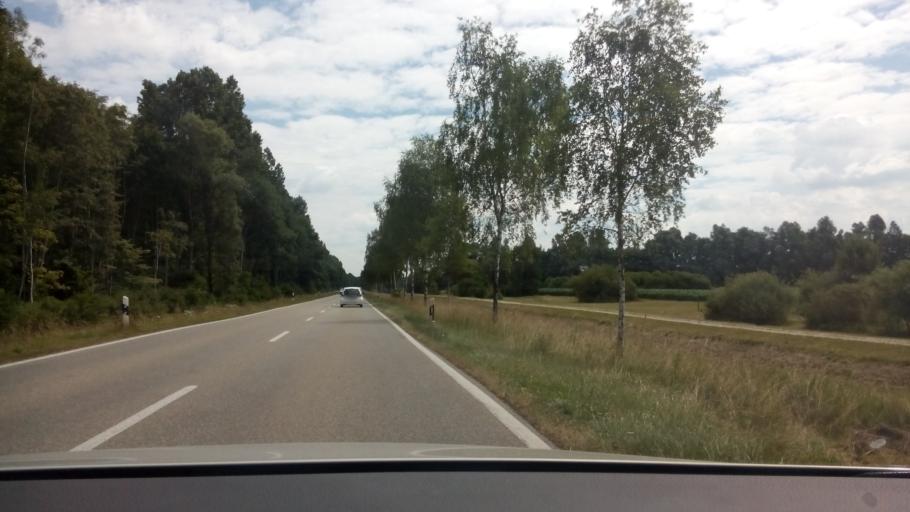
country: DE
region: Bavaria
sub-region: Upper Bavaria
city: Marzling
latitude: 48.3737
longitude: 11.7953
